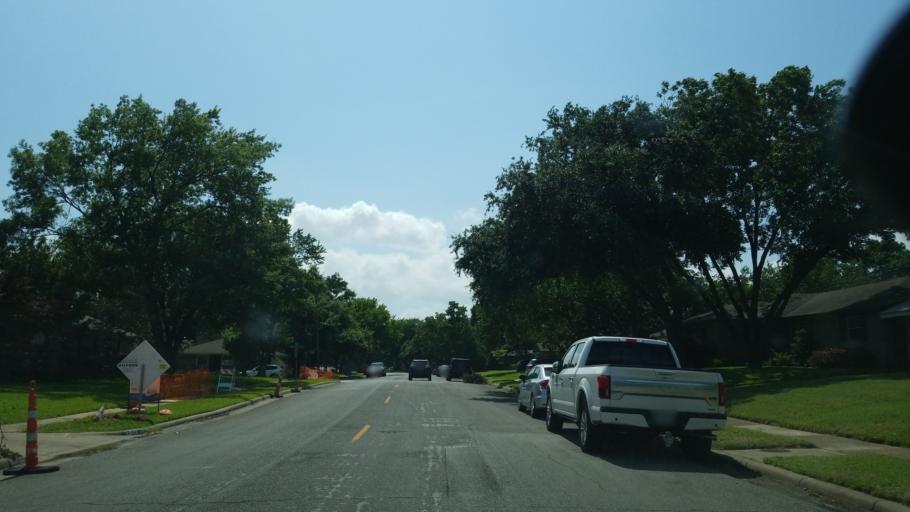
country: US
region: Texas
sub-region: Dallas County
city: Farmers Branch
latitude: 32.8878
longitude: -96.8580
